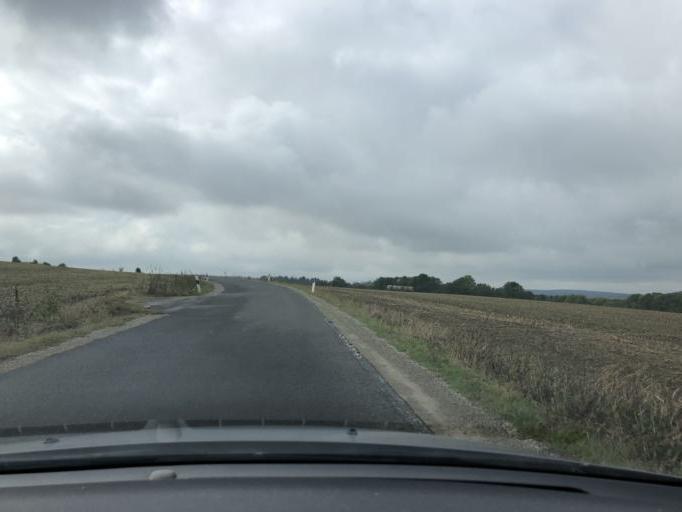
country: DE
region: Thuringia
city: Kreuzebra
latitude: 51.3430
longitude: 10.2435
